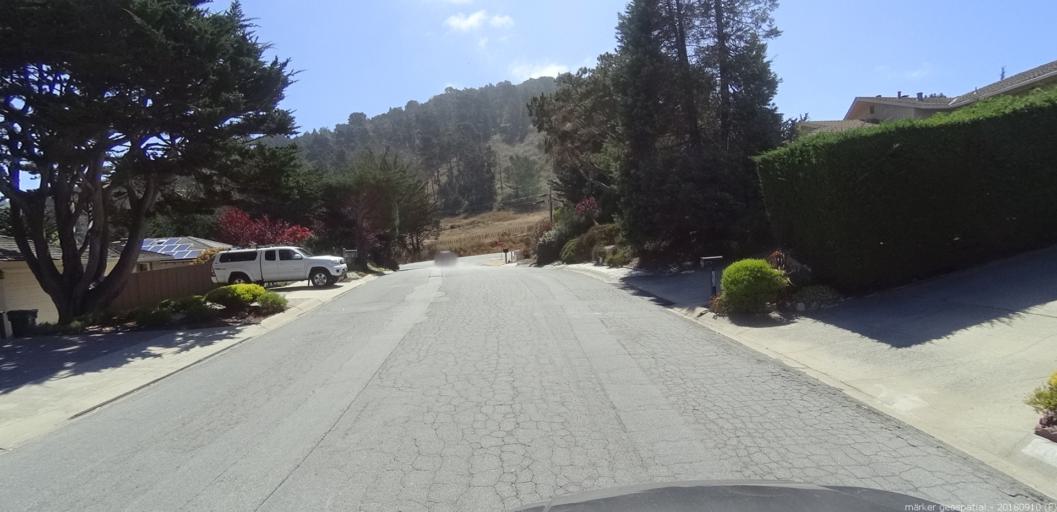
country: US
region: California
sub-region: Monterey County
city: Carmel-by-the-Sea
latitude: 36.5296
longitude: -121.9199
